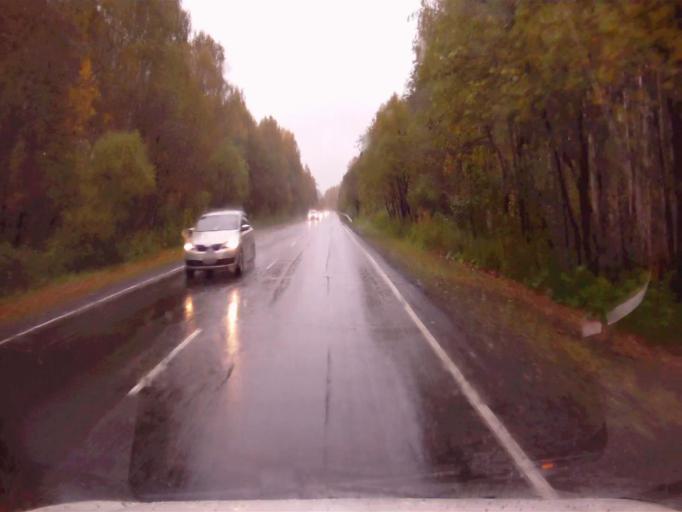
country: RU
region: Chelyabinsk
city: Verkhniy Ufaley
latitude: 55.9392
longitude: 60.4114
